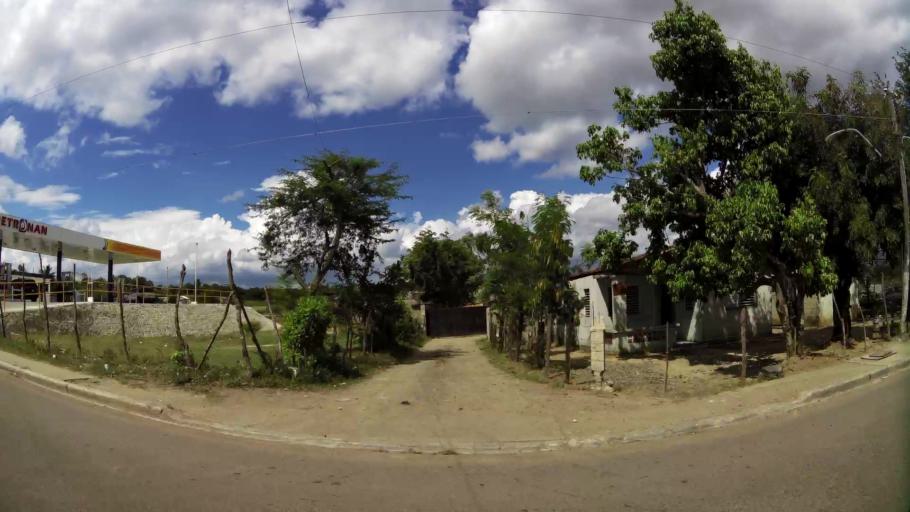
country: DO
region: Santiago
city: Santiago de los Caballeros
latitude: 19.4070
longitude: -70.6678
